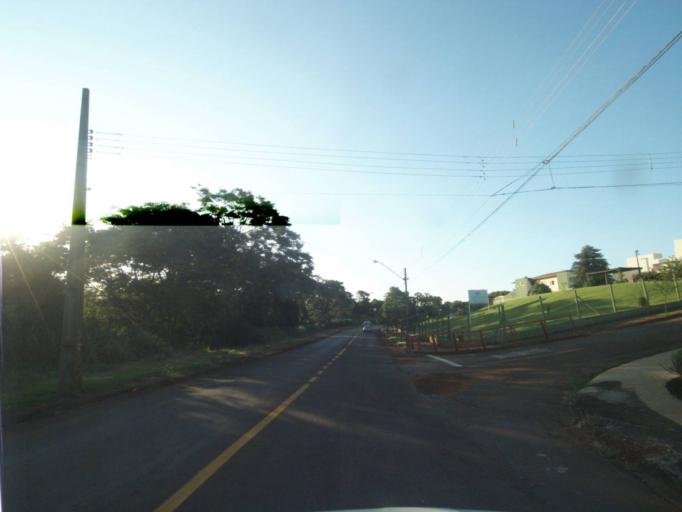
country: BR
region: Parana
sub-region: Londrina
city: Londrina
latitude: -23.3494
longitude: -51.1933
